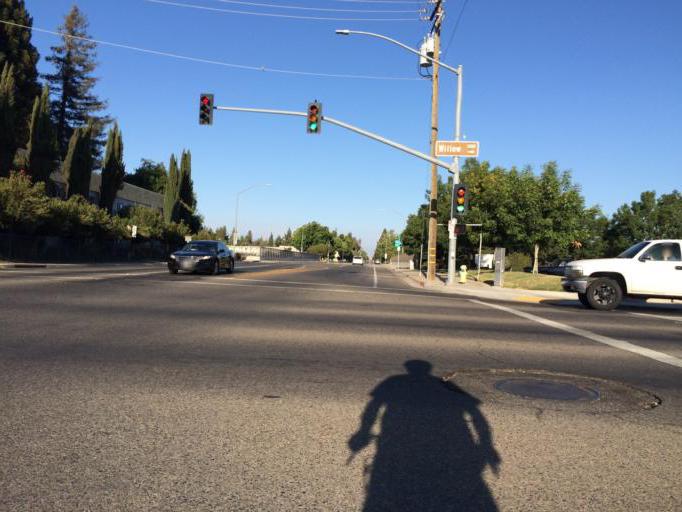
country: US
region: California
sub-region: Fresno County
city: Clovis
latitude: 36.8157
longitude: -119.7274
